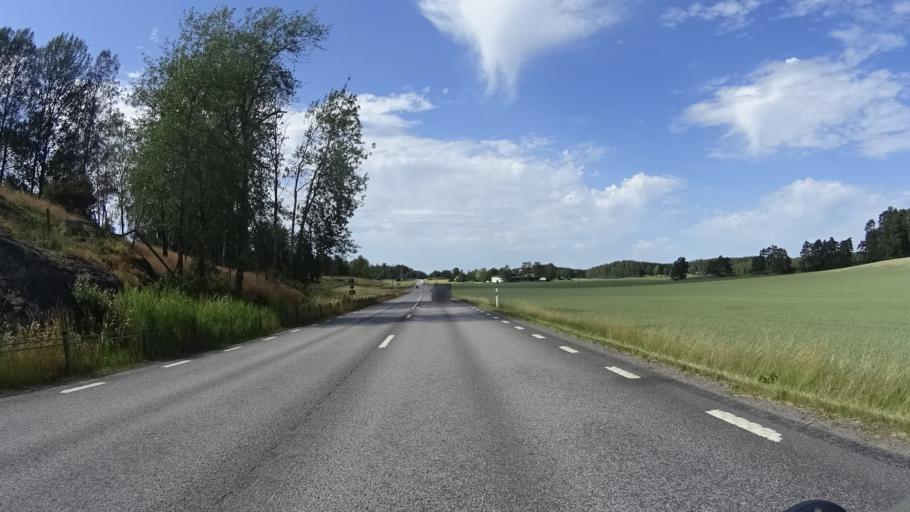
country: SE
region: OEstergoetland
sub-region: Linkopings Kommun
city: Linghem
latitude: 58.3471
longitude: 15.8409
